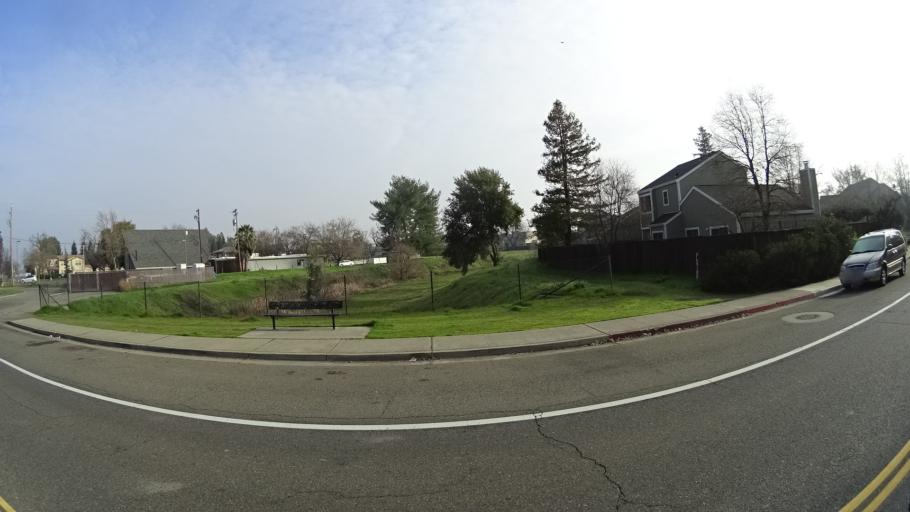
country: US
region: California
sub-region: Yolo County
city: Davis
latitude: 38.5676
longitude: -121.7670
